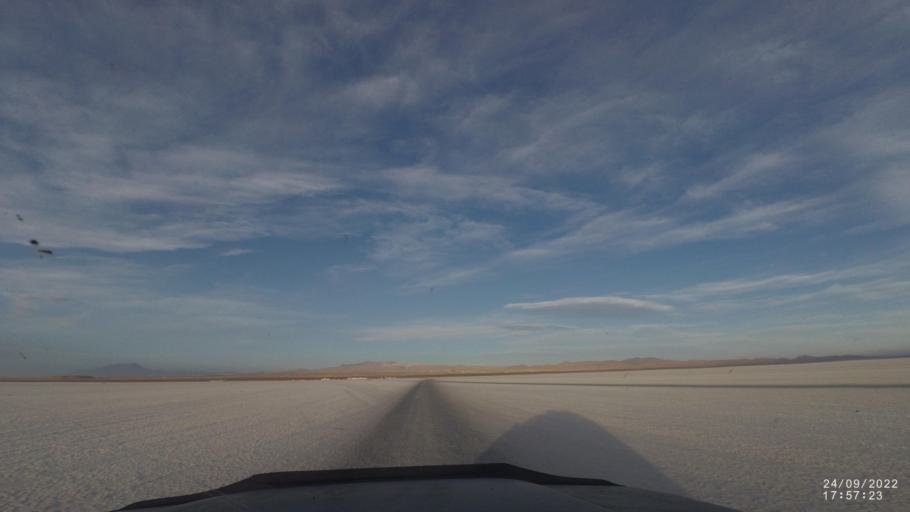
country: BO
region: Potosi
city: Colchani
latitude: -20.3206
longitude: -66.9937
